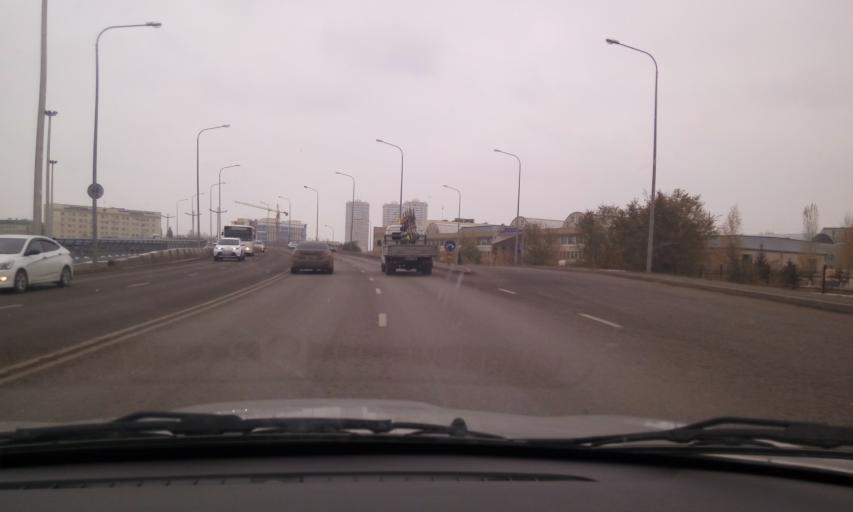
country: KZ
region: Astana Qalasy
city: Astana
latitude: 51.1557
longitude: 71.4670
